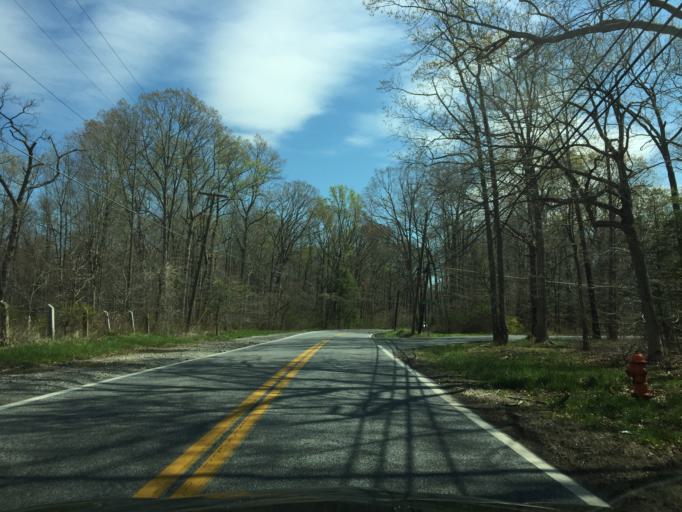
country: US
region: Maryland
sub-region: Baltimore County
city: Edgemere
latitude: 39.2659
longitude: -76.4209
